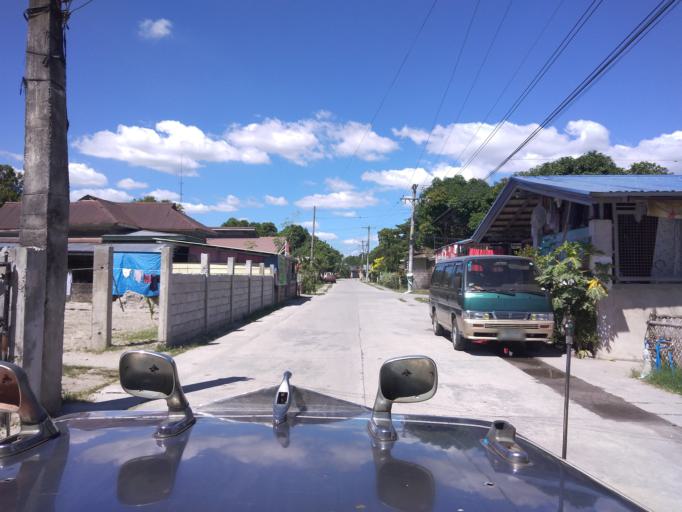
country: PH
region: Central Luzon
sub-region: Province of Pampanga
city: Magliman
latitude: 15.0342
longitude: 120.6481
